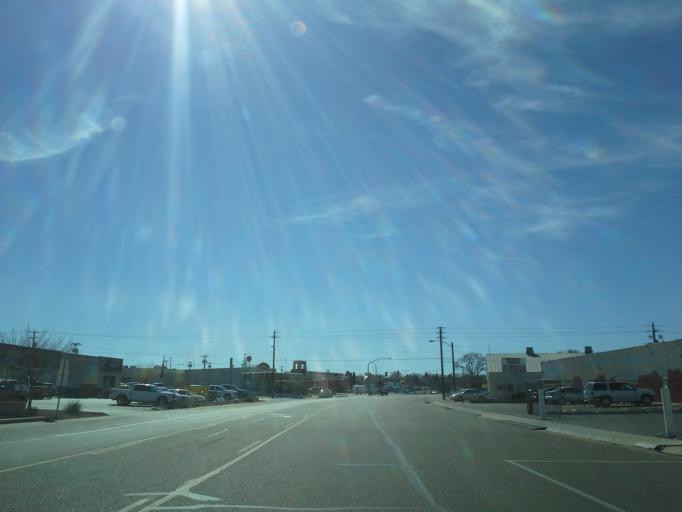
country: US
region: Arizona
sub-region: Coconino County
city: Page
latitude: 36.9206
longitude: -111.4586
